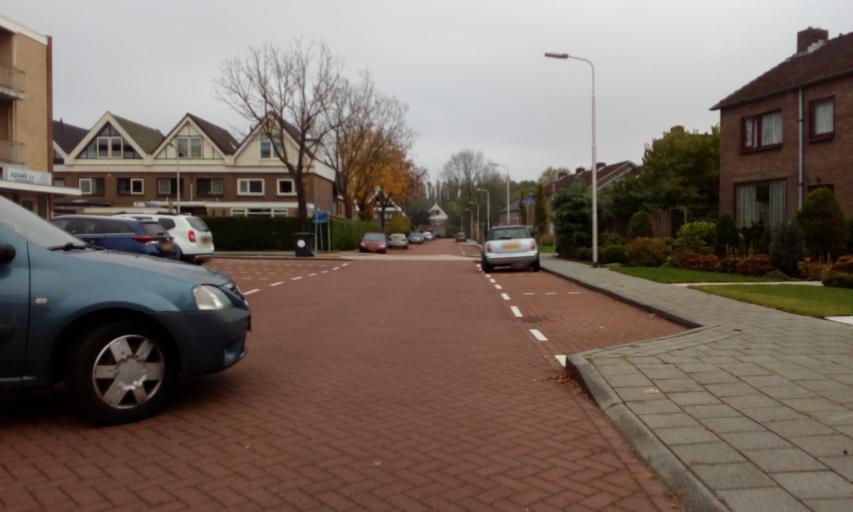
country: NL
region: South Holland
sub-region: Gemeente Lansingerland
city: Berkel en Rodenrijs
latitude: 51.9985
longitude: 4.4831
